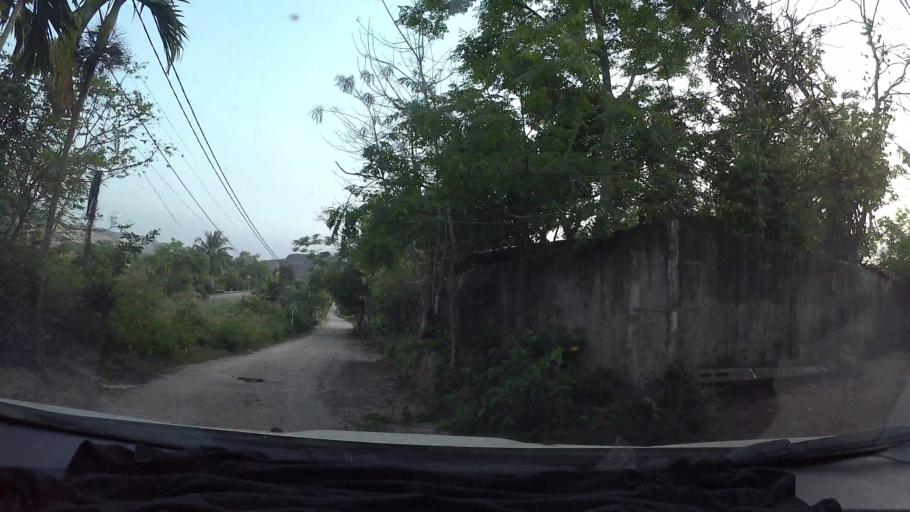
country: VN
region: Da Nang
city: Lien Chieu
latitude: 16.0558
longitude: 108.1070
